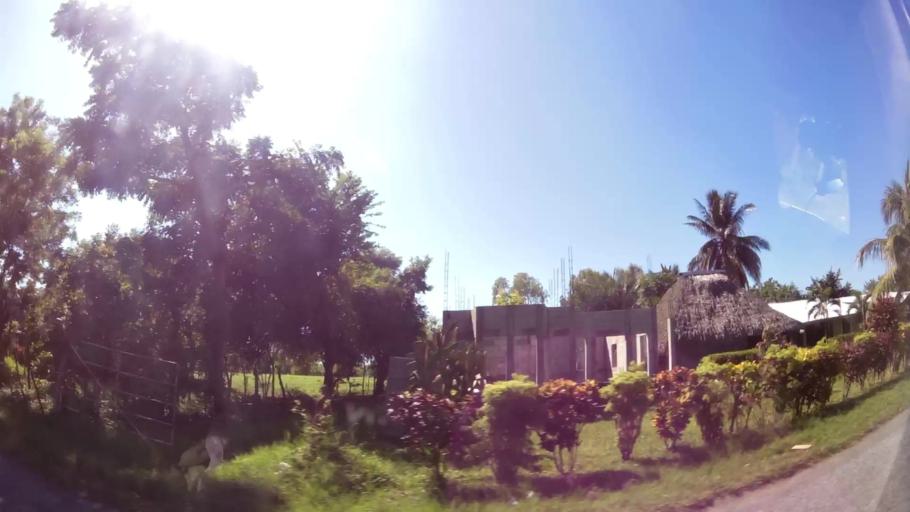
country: GT
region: Escuintla
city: Iztapa
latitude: 13.9194
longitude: -90.5606
